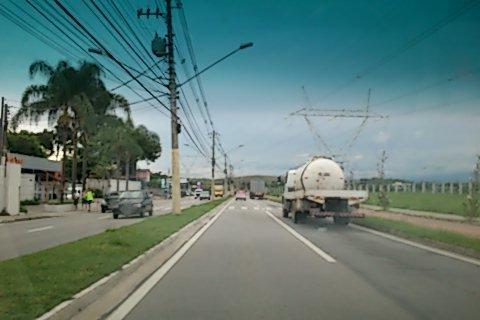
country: BR
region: Sao Paulo
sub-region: Sao Jose Dos Campos
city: Sao Jose dos Campos
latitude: -23.1963
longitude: -45.9183
